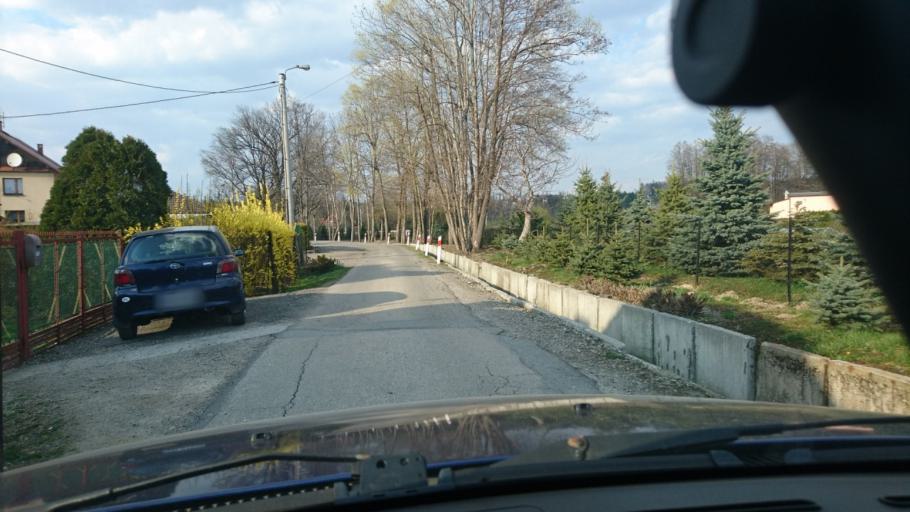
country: PL
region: Silesian Voivodeship
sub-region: Powiat bielski
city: Mazancowice
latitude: 49.8520
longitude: 18.9831
